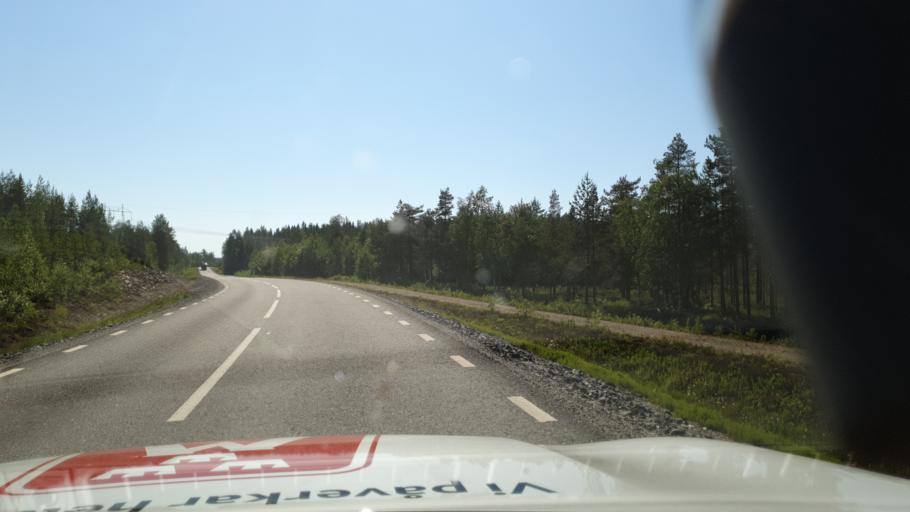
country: SE
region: Vaesterbotten
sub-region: Umea Kommun
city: Ersmark
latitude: 64.2553
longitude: 20.1615
